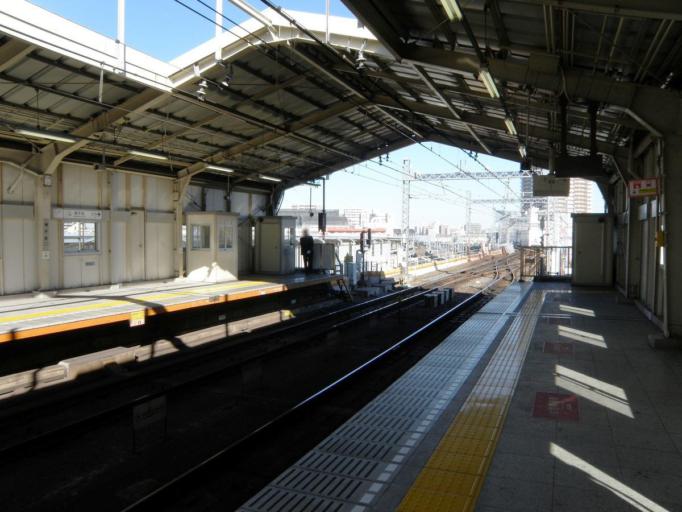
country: JP
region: Saitama
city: Soka
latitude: 35.7348
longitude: 139.8002
